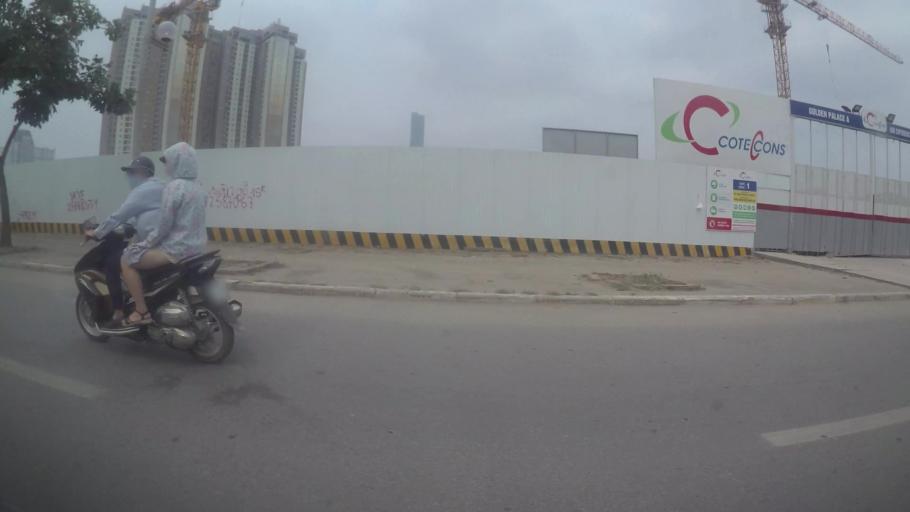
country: VN
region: Ha Noi
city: Thanh Xuan
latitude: 21.0092
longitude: 105.7740
